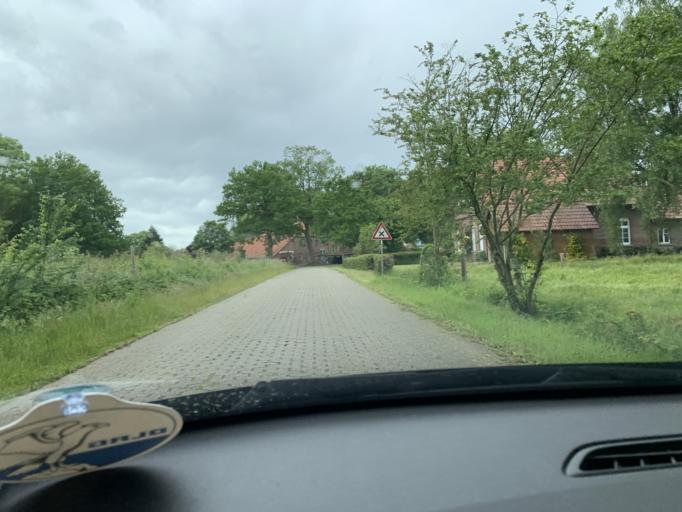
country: DE
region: Lower Saxony
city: Zetel
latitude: 53.3977
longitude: 7.9417
